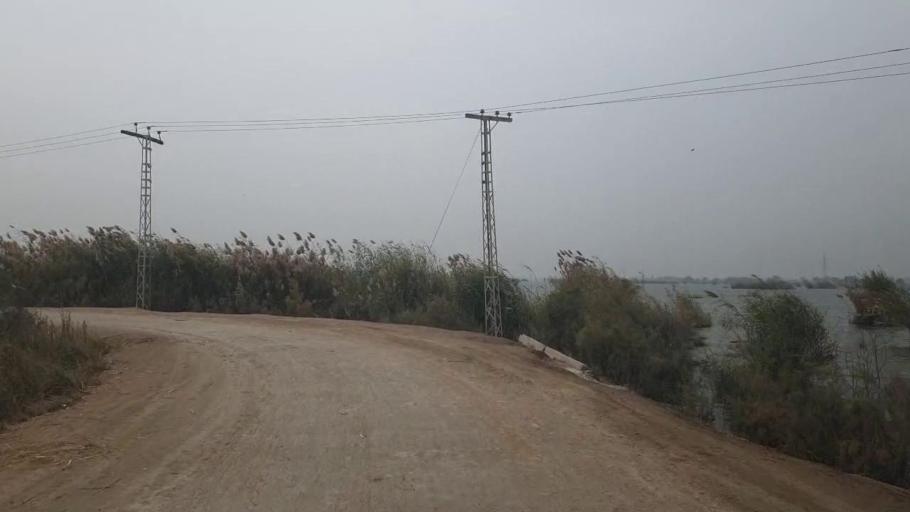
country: PK
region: Sindh
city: Shahdadpur
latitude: 25.8667
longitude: 68.6253
